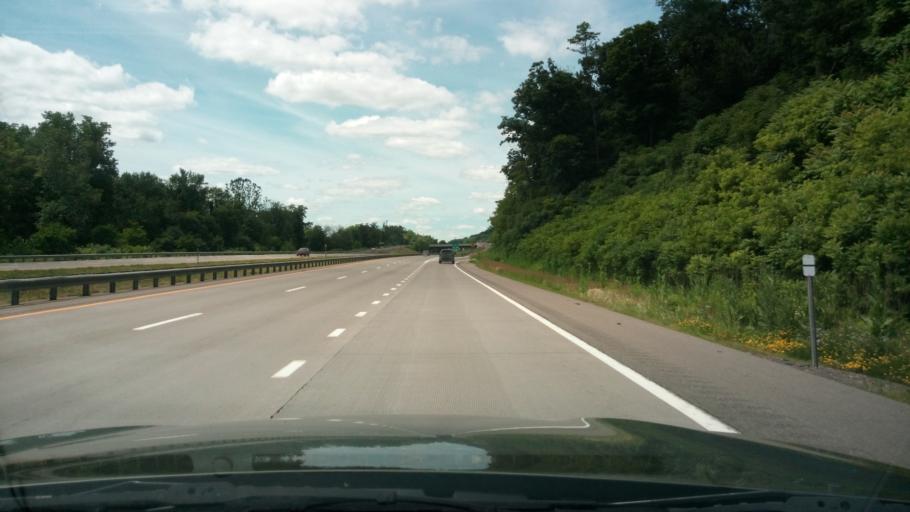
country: US
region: New York
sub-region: Chemung County
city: Elmira
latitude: 42.0868
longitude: -76.7799
